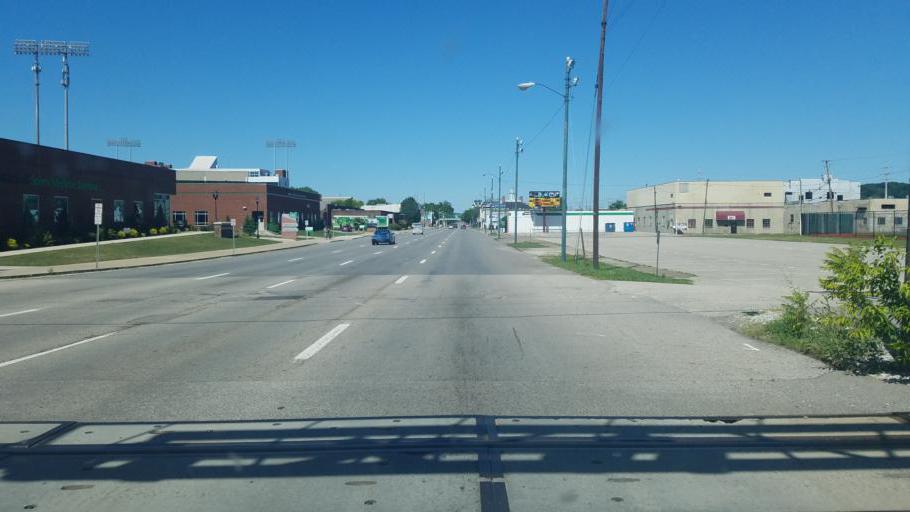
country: US
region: West Virginia
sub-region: Cabell County
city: Huntington
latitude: 38.4265
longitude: -82.4185
